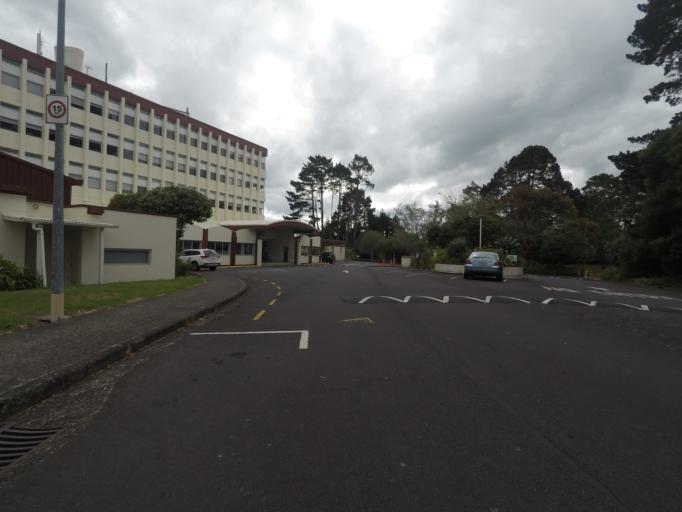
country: NZ
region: Auckland
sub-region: Auckland
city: Auckland
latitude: -36.8737
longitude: 174.7214
